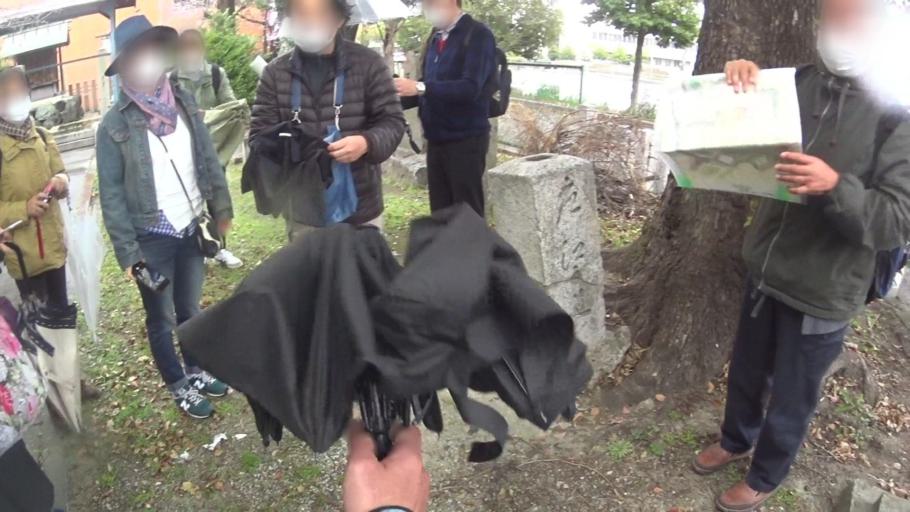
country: JP
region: Aichi
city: Nagoya-shi
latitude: 35.1169
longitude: 136.9117
